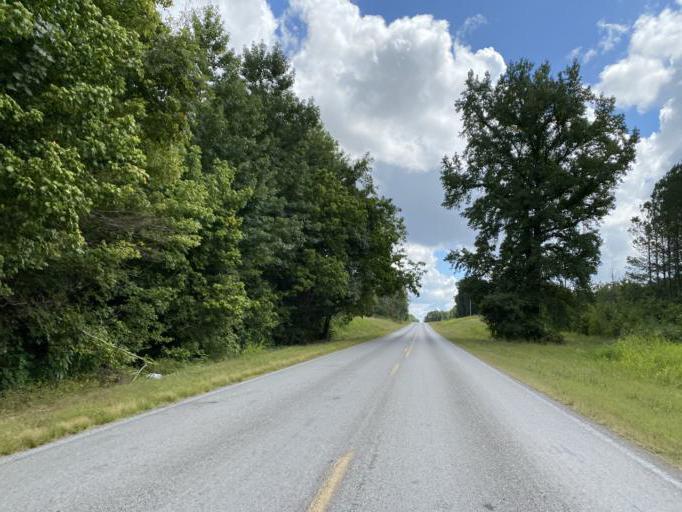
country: US
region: Mississippi
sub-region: Panola County
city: Como
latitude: 34.5105
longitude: -90.0171
